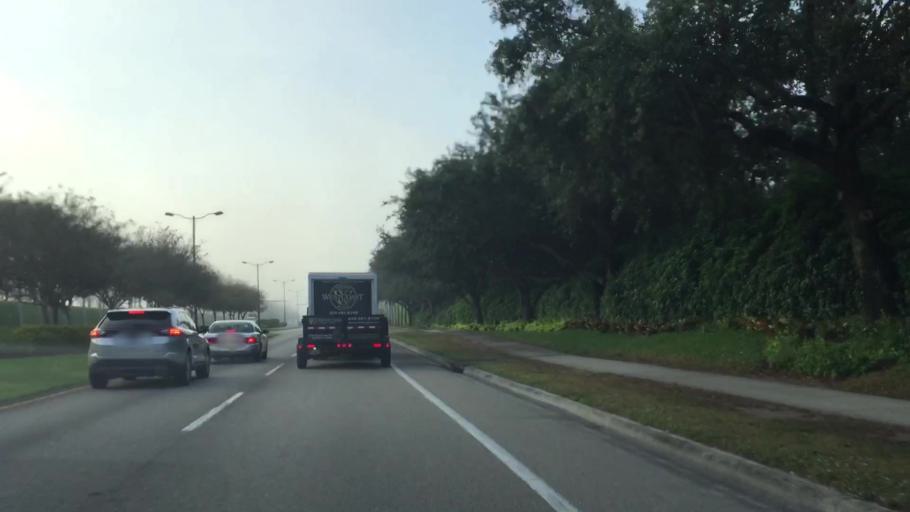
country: US
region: Florida
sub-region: Lee County
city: Three Oaks
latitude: 26.4761
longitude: -81.7868
